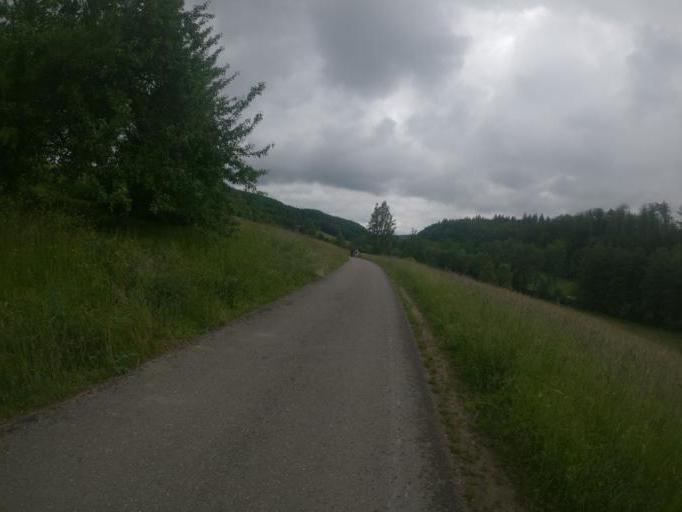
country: DE
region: Baden-Wuerttemberg
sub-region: Regierungsbezirk Stuttgart
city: Ebersbach an der Fils
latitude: 48.7525
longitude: 9.5358
